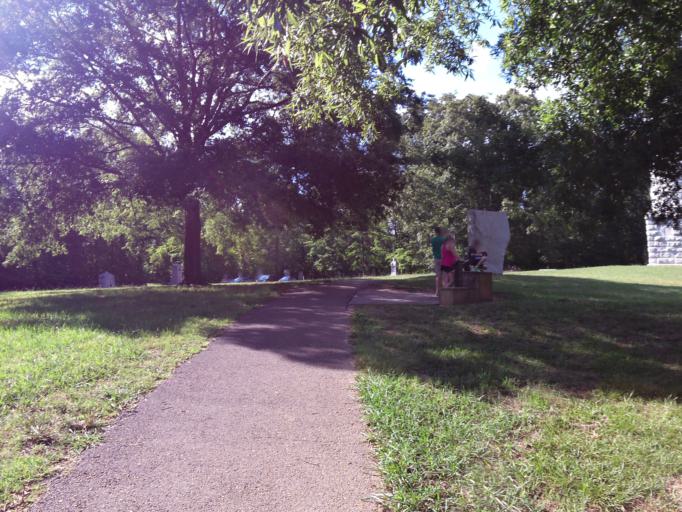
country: US
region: Georgia
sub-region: Walker County
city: Chickamauga
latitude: 34.9070
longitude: -85.2725
